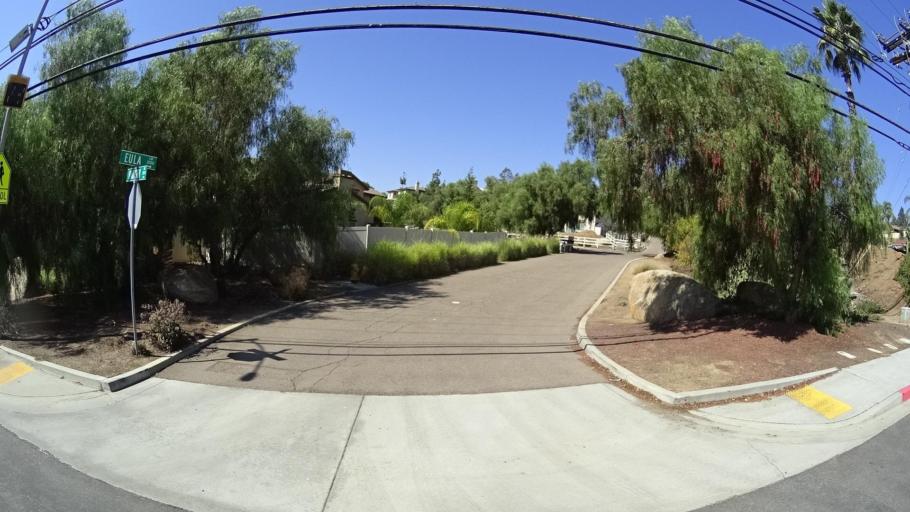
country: US
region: California
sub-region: San Diego County
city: Granite Hills
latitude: 32.8032
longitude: -116.9020
